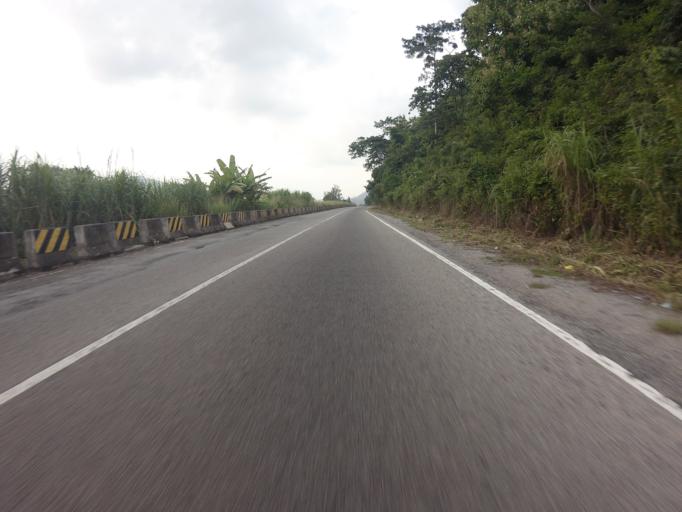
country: GH
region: Volta
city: Ho
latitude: 6.6333
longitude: 0.4646
